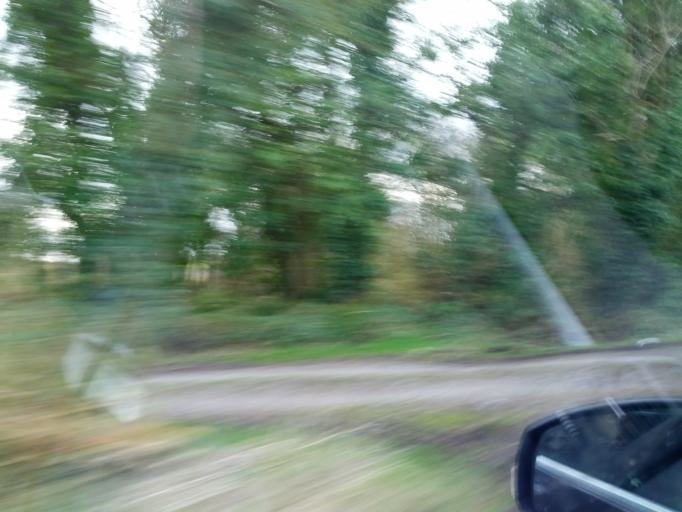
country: IE
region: Connaught
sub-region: County Galway
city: Athenry
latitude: 53.4896
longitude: -8.5913
